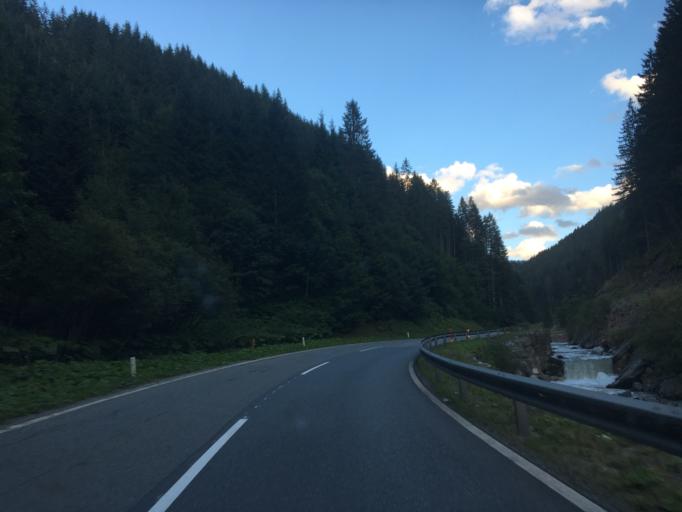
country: AT
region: Styria
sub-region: Politischer Bezirk Liezen
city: Trieben
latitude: 47.4585
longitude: 14.4886
